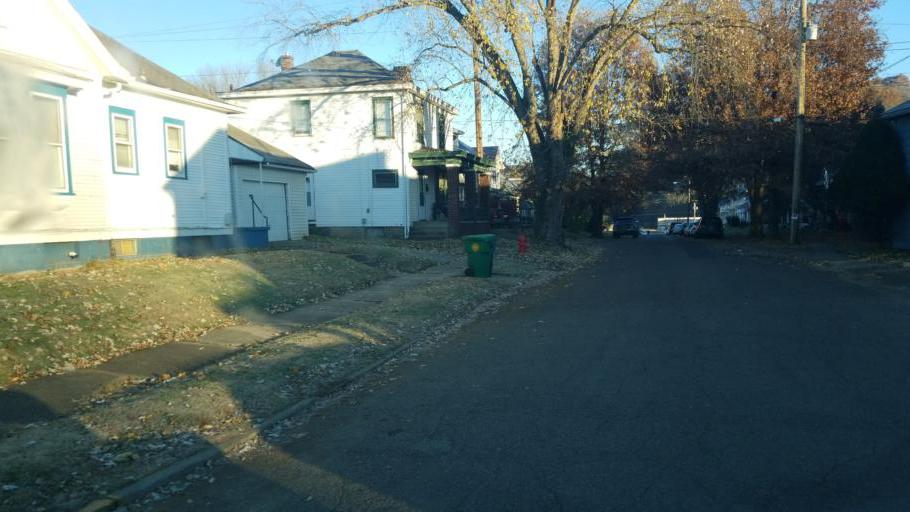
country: US
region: Kentucky
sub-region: Greenup County
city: South Shore
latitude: 38.7424
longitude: -82.9720
